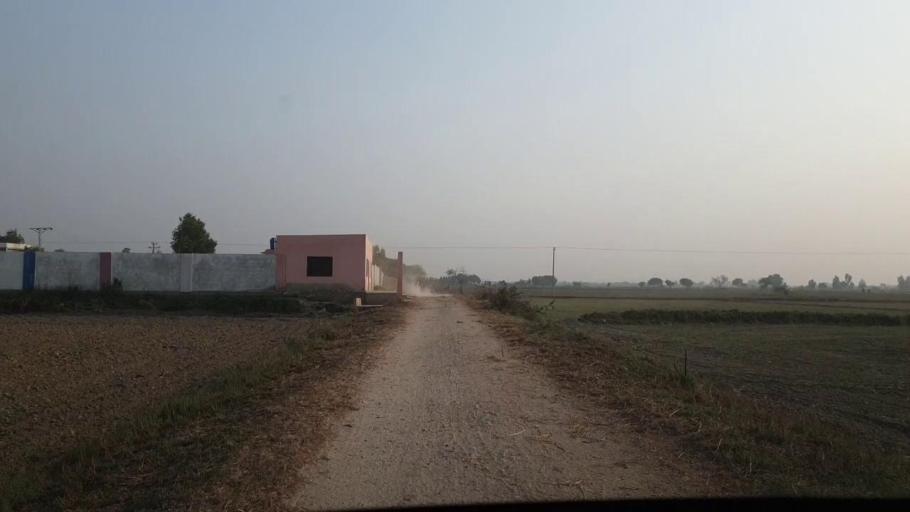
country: PK
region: Sindh
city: Chuhar Jamali
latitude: 24.2565
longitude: 68.1130
